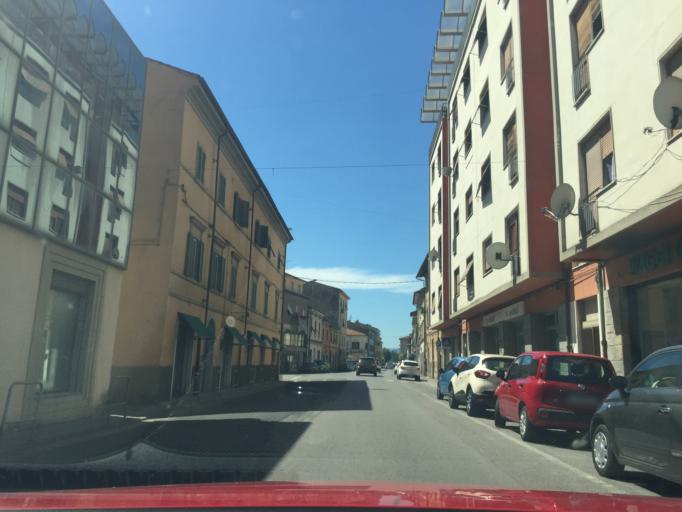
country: IT
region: Tuscany
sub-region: Province of Pisa
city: Pontedera
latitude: 43.6663
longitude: 10.6422
